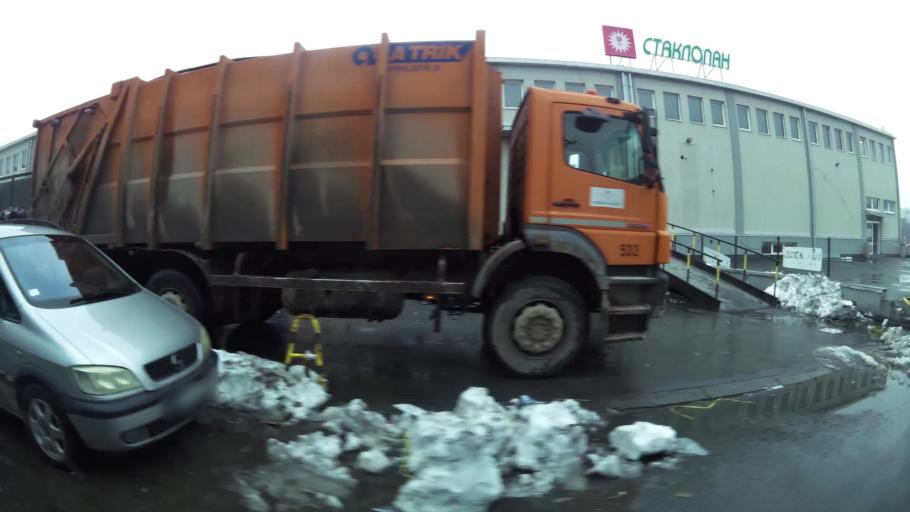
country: RS
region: Central Serbia
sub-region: Belgrade
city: Vozdovac
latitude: 44.7684
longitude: 20.4869
